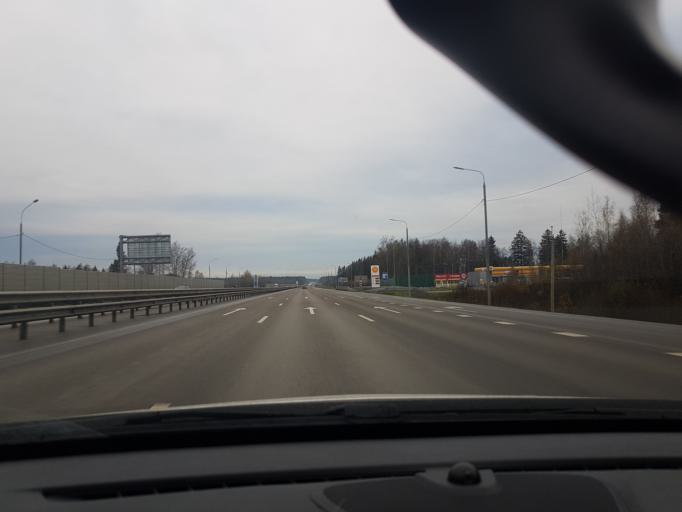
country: RU
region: Moskovskaya
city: Kostrovo
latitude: 55.8564
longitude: 36.7641
